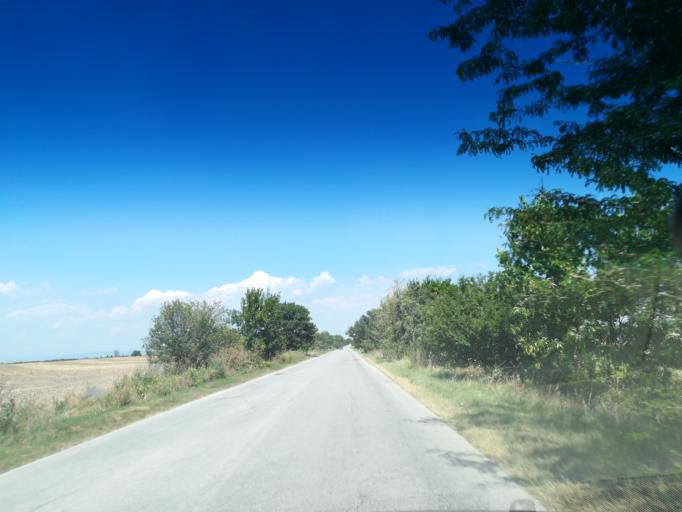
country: BG
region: Plovdiv
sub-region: Obshtina Sadovo
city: Sadovo
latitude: 42.0461
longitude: 25.1402
